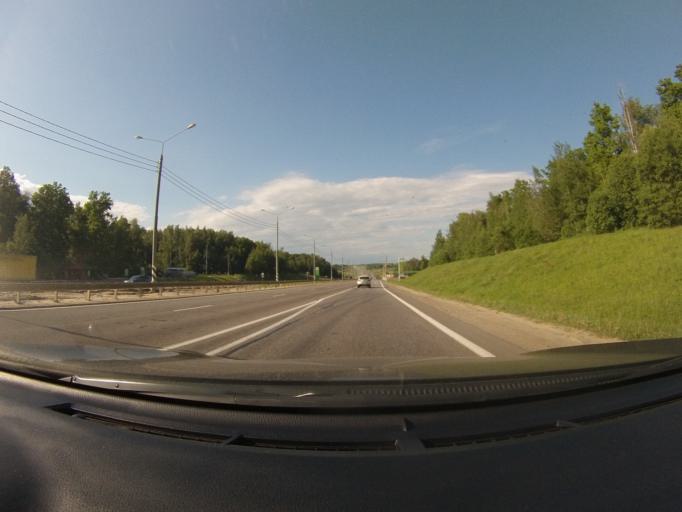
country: RU
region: Tula
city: Leninskiy
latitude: 54.4140
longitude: 37.5007
